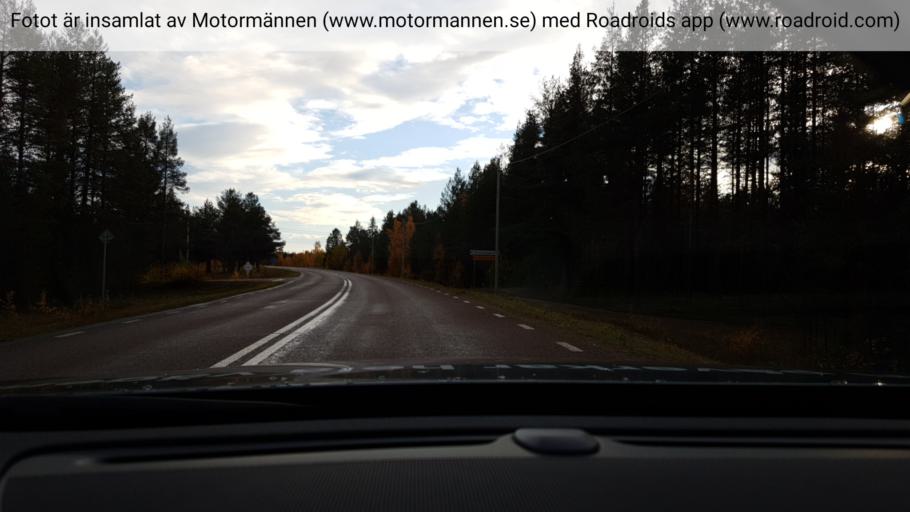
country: SE
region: Norrbotten
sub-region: Pajala Kommun
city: Pajala
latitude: 67.1640
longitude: 22.6348
